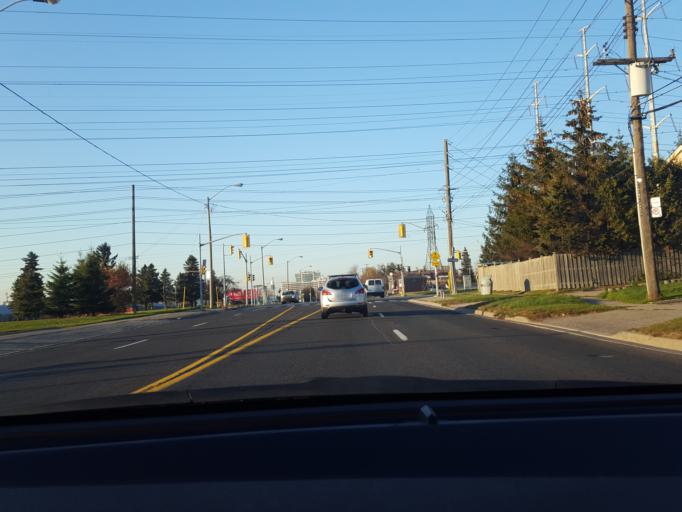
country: CA
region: Ontario
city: Scarborough
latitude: 43.7381
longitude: -79.2809
